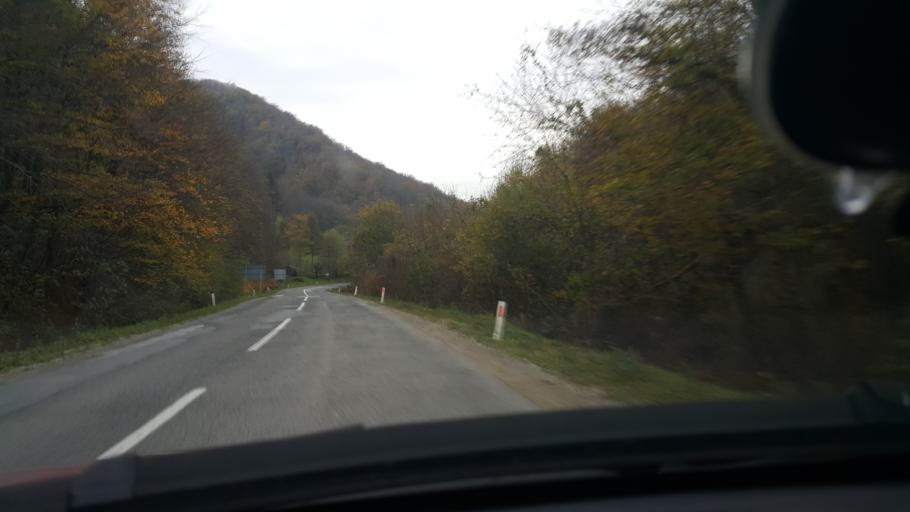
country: SI
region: Bistrica ob Sotli
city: Bistrica ob Sotli
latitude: 46.0437
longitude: 15.6856
